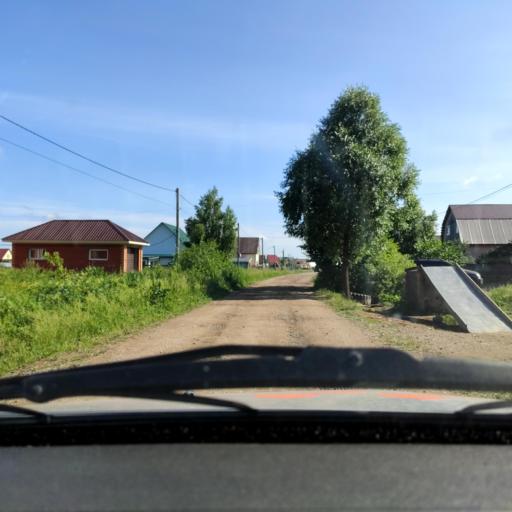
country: RU
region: Bashkortostan
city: Iglino
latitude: 54.7983
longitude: 56.2982
